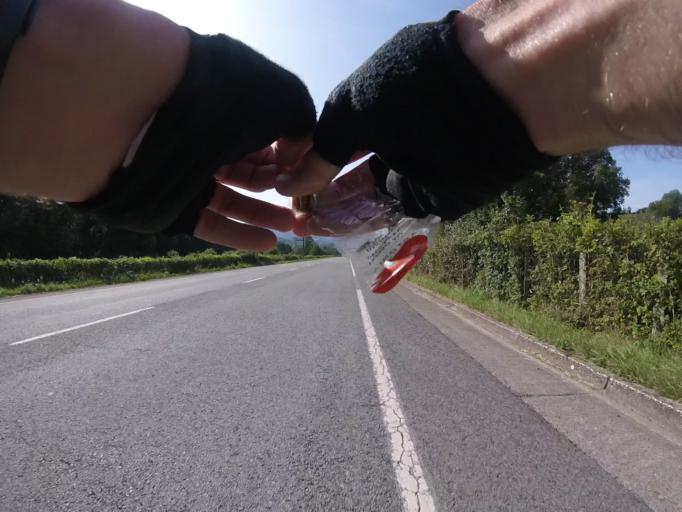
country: ES
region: Navarre
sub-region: Provincia de Navarra
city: Zugarramurdi
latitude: 43.1893
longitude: -1.4868
